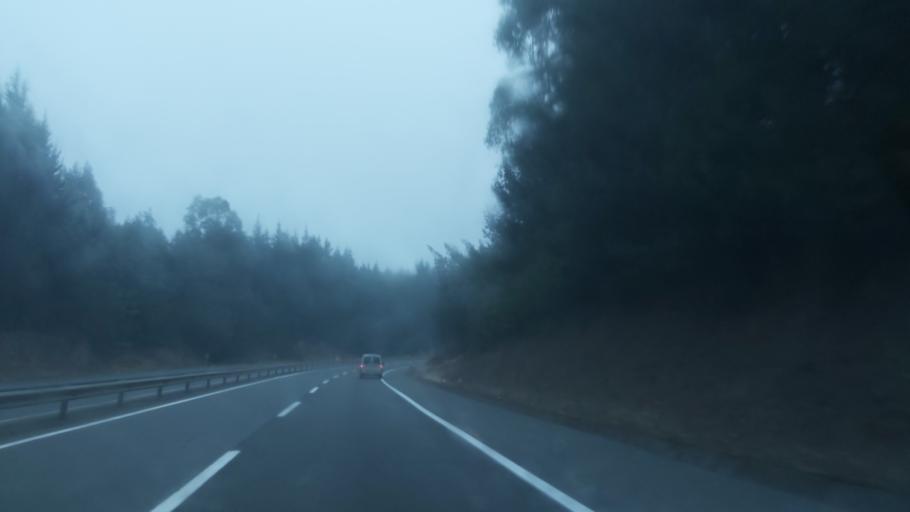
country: CL
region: Biobio
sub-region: Provincia de Concepcion
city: Penco
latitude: -36.7403
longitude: -72.9024
